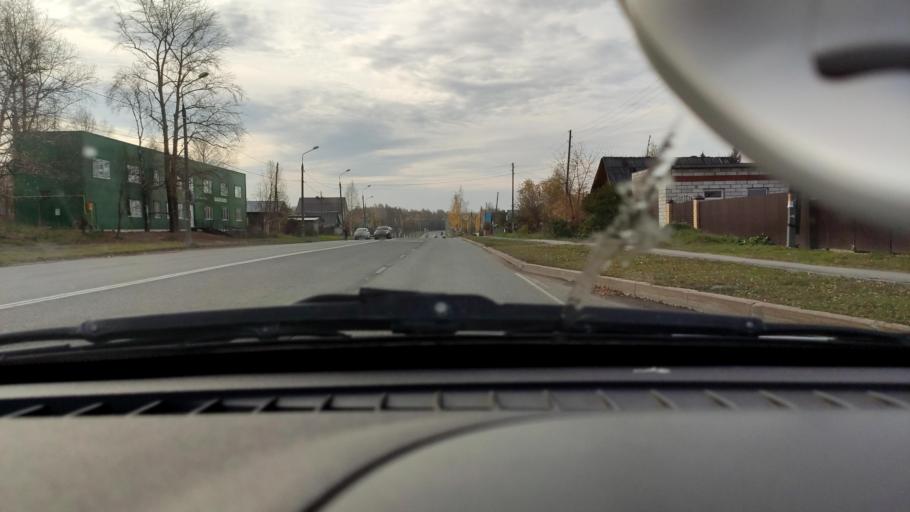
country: RU
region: Perm
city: Polazna
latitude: 58.1164
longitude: 56.4013
